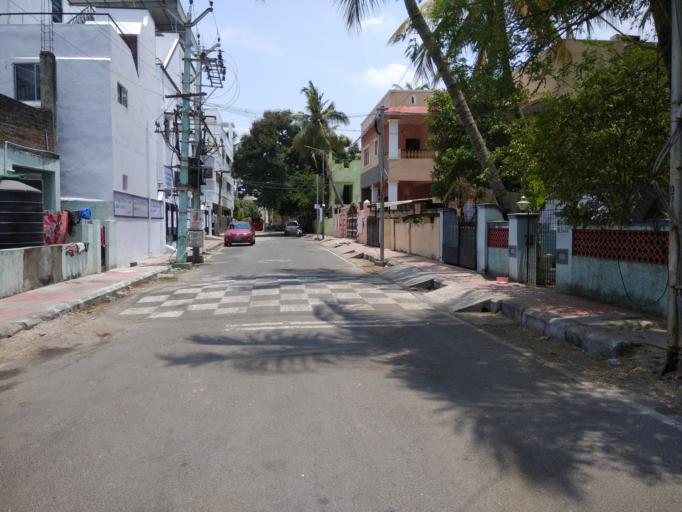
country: IN
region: Tamil Nadu
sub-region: Kancheepuram
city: Saint Thomas Mount
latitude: 12.9894
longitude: 80.1998
